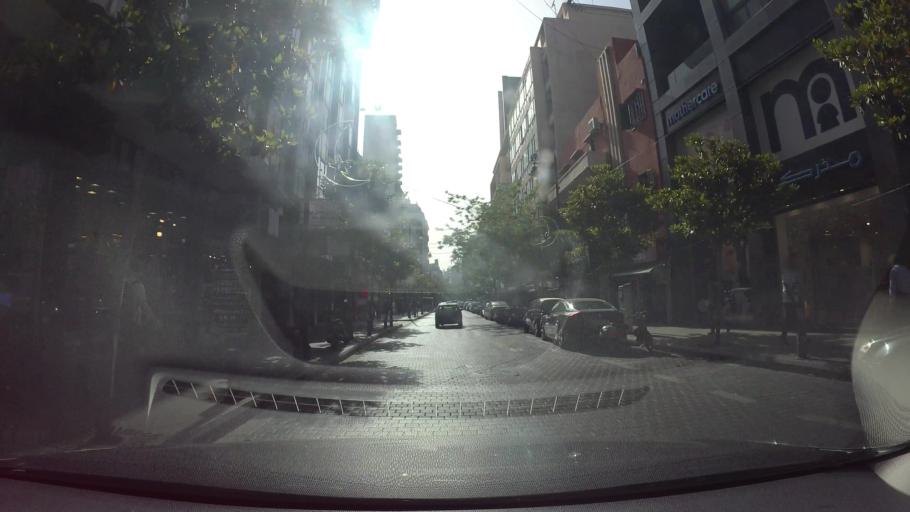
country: LB
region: Beyrouth
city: Ra's Bayrut
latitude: 33.8956
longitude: 35.4821
